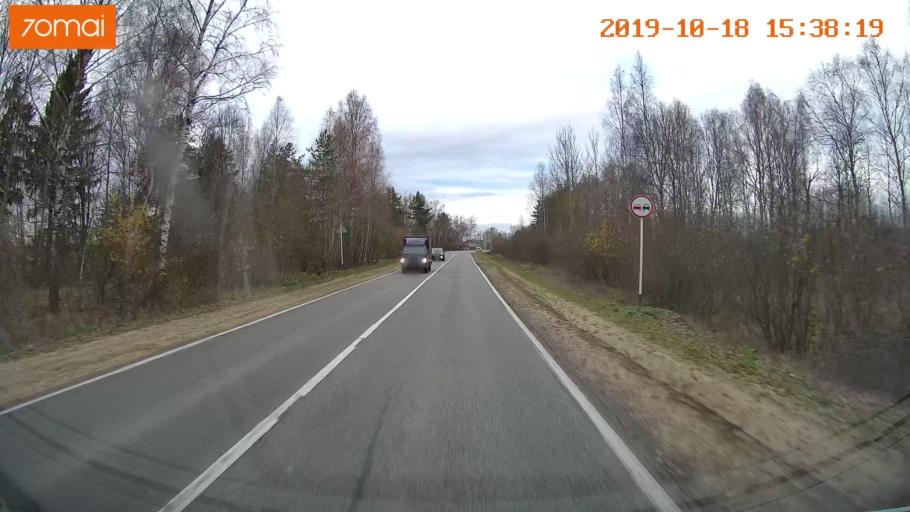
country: RU
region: Vladimir
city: Golovino
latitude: 55.9095
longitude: 40.6078
